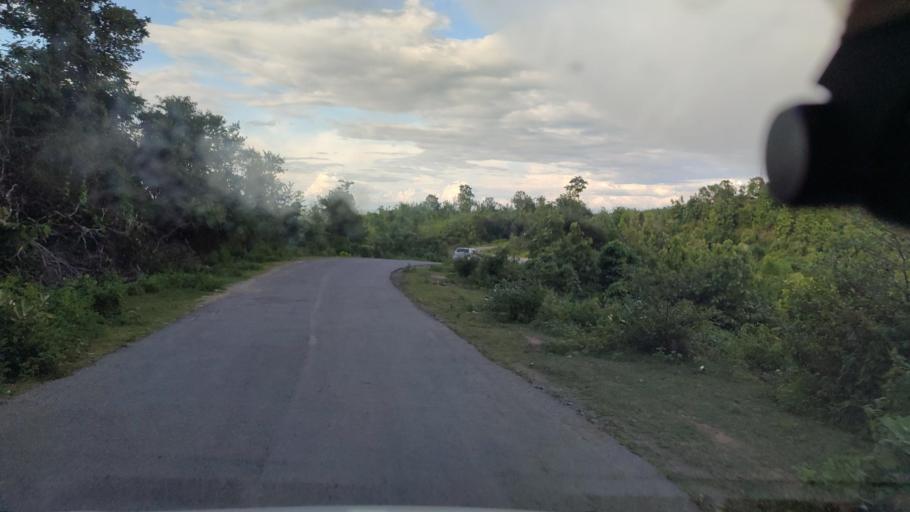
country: MM
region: Magway
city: Taungdwingyi
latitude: 20.0151
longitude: 95.8288
